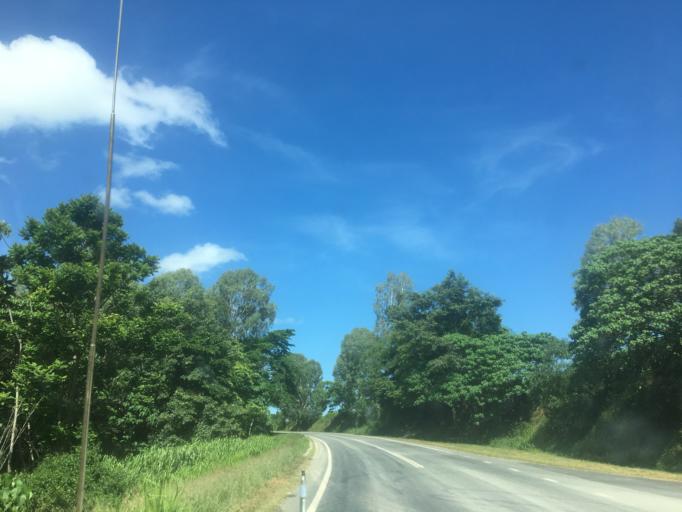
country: AU
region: Queensland
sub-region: Cairns
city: Woree
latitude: -17.0684
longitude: 145.7459
